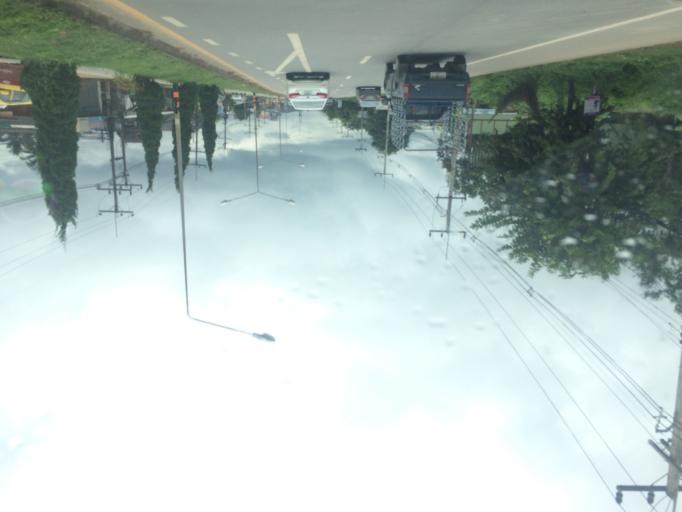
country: TH
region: Chiang Rai
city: Chiang Rai
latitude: 20.0155
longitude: 99.8694
